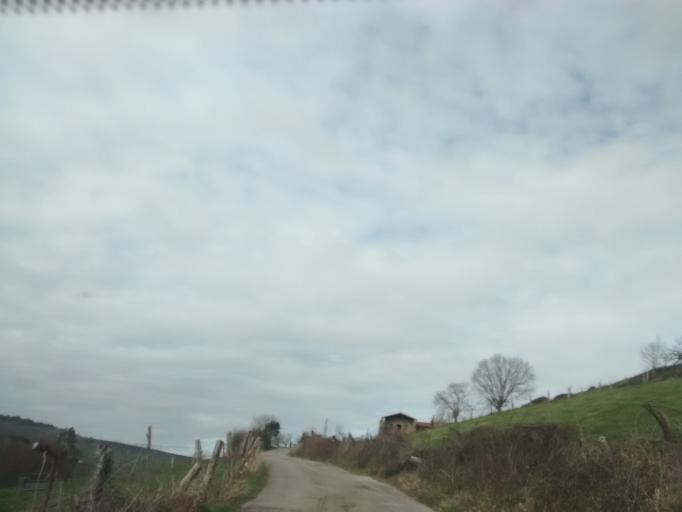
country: ES
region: Cantabria
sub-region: Provincia de Cantabria
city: Lierganes
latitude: 43.3253
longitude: -3.7343
